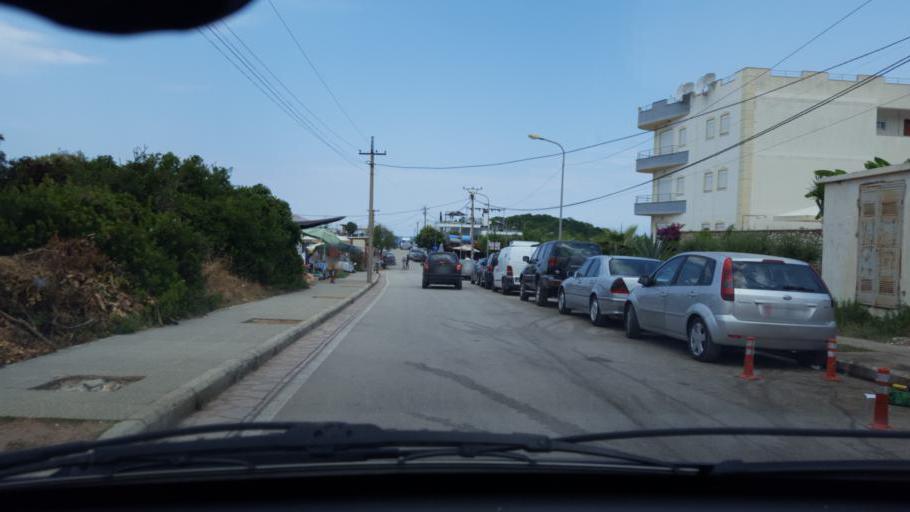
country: AL
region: Vlore
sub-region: Rrethi i Sarandes
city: Xarre
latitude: 39.7715
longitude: 19.9994
